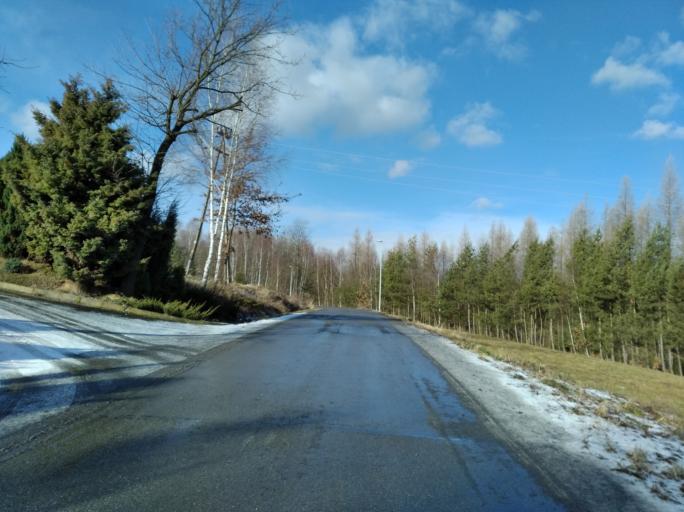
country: PL
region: Subcarpathian Voivodeship
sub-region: Powiat strzyzowski
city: Strzyzow
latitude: 49.8972
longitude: 21.7730
